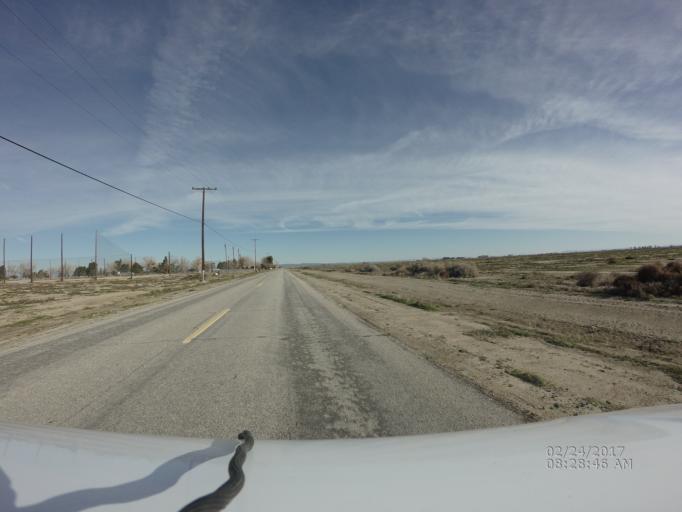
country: US
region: California
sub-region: Los Angeles County
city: Lancaster
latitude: 34.7388
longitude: -118.0232
